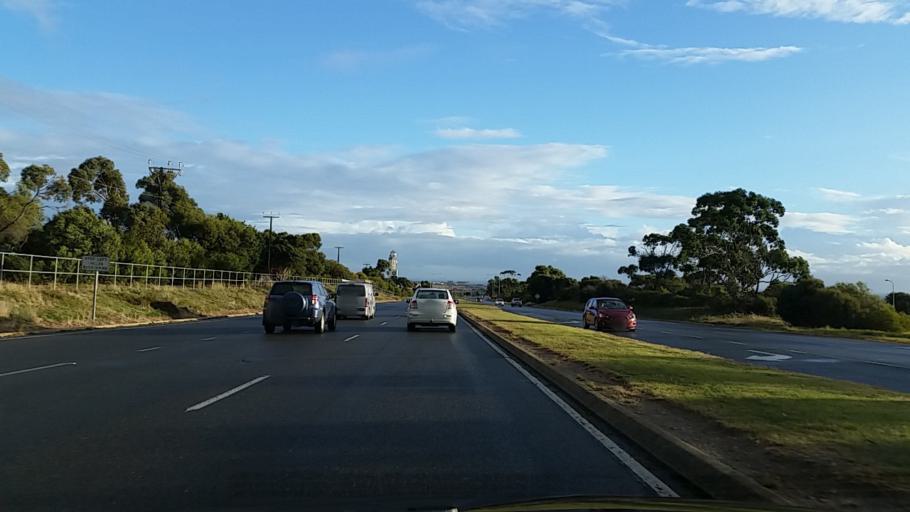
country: AU
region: South Australia
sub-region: Marion
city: Happy Valley
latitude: -35.0724
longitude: 138.5252
